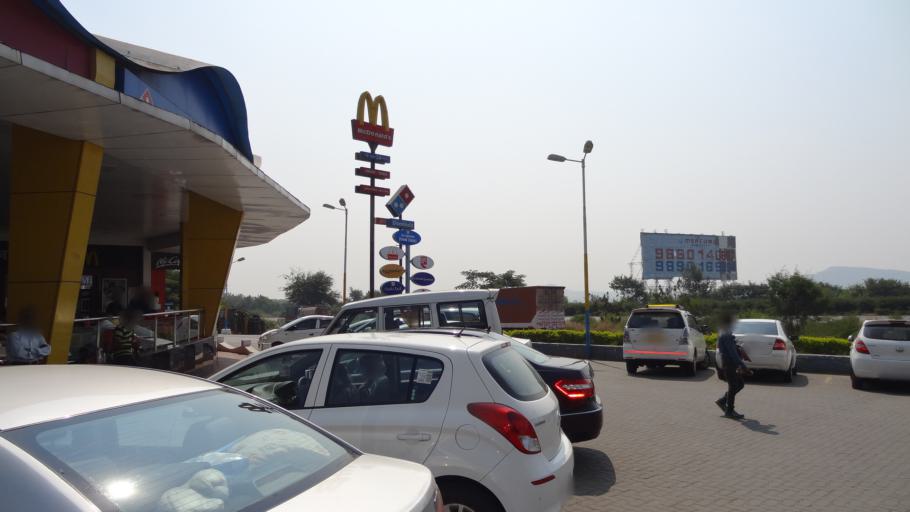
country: IN
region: Maharashtra
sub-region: Pune Division
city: Wadgaon
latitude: 18.7118
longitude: 73.6523
